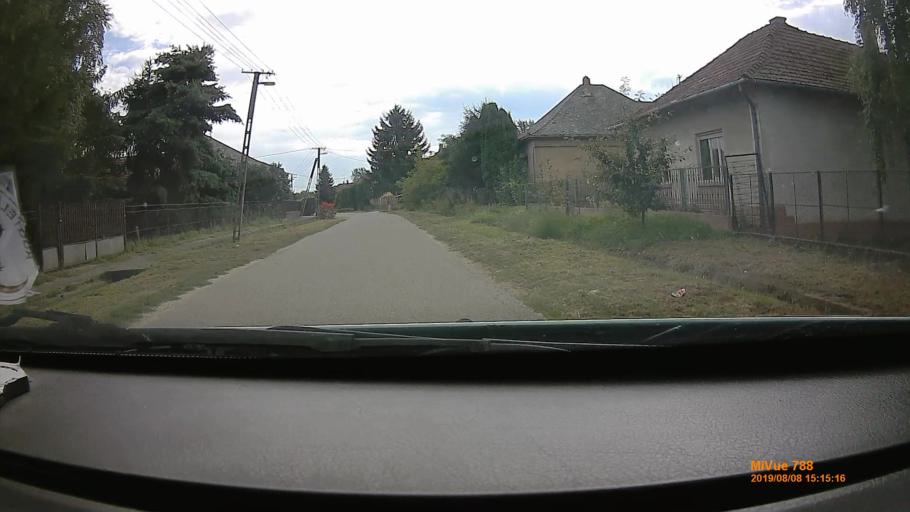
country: HU
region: Szabolcs-Szatmar-Bereg
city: Tunyogmatolcs
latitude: 47.9692
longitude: 22.4581
